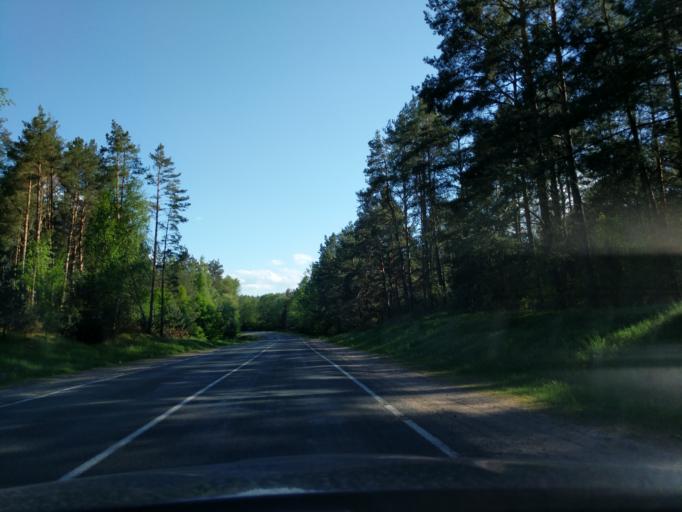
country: BY
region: Minsk
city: Myadzyel
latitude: 54.8458
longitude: 26.9261
